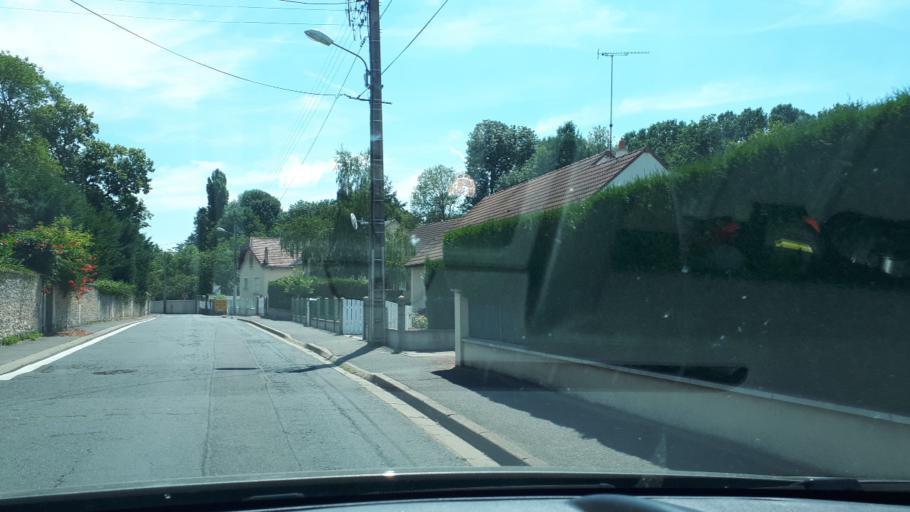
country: FR
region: Centre
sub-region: Departement du Loir-et-Cher
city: Naveil
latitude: 47.8018
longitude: 1.0411
